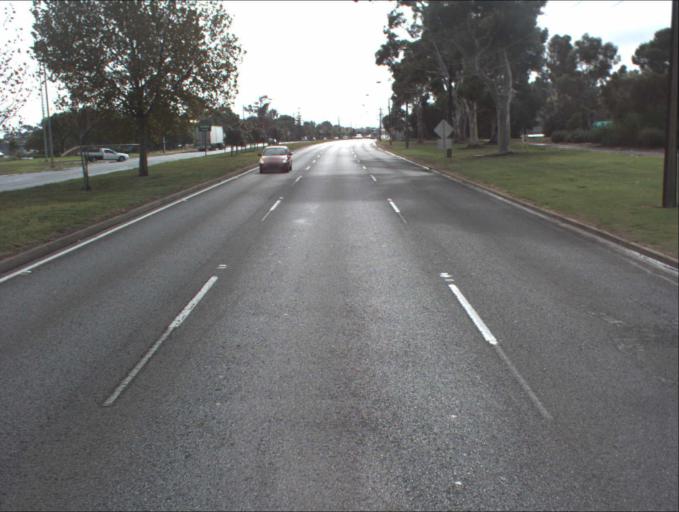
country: AU
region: South Australia
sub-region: Port Adelaide Enfield
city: Enfield
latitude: -34.8345
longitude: 138.6102
